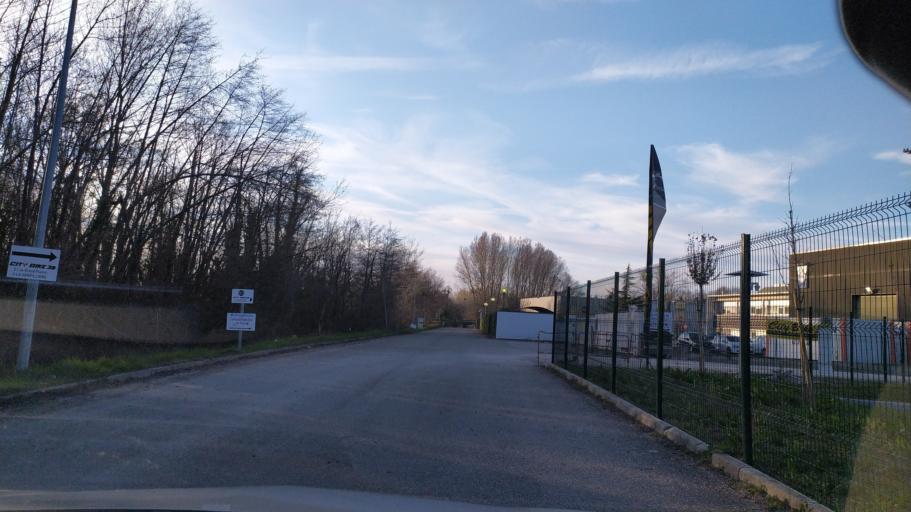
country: FR
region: Rhone-Alpes
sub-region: Departement de l'Isere
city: La Verpilliere
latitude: 45.6322
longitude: 5.1572
